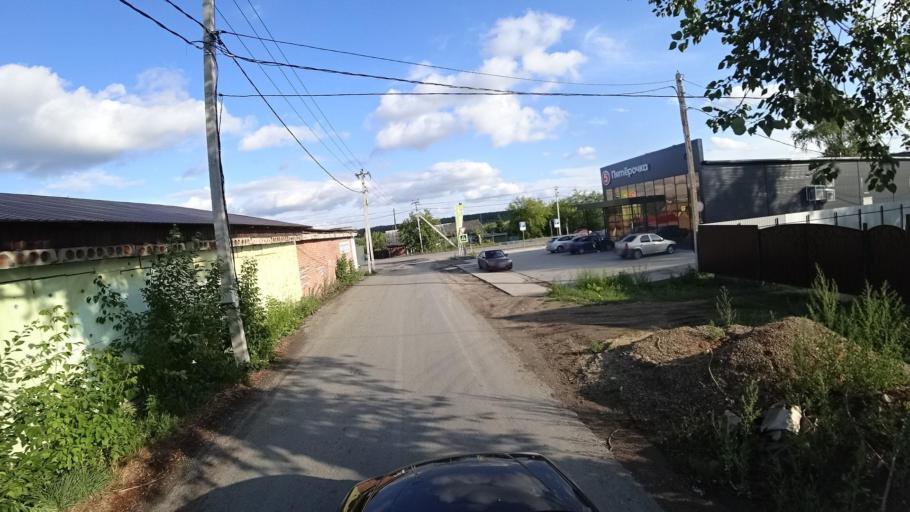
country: RU
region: Sverdlovsk
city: Obukhovskoye
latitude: 56.8469
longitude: 62.6547
